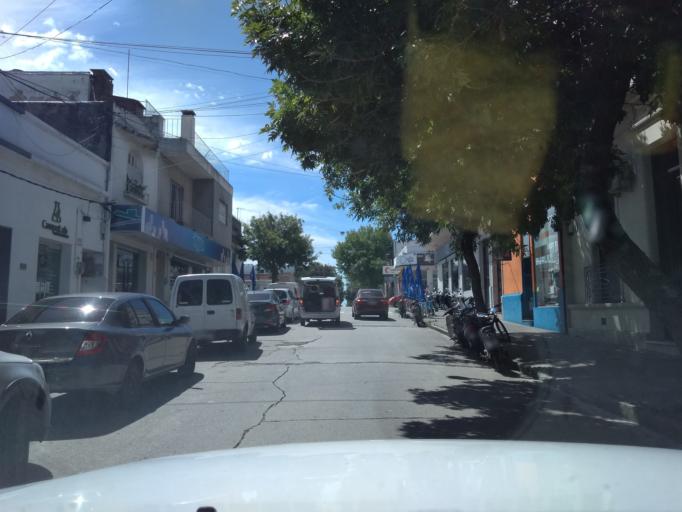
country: UY
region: Florida
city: Florida
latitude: -34.0974
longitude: -56.2152
